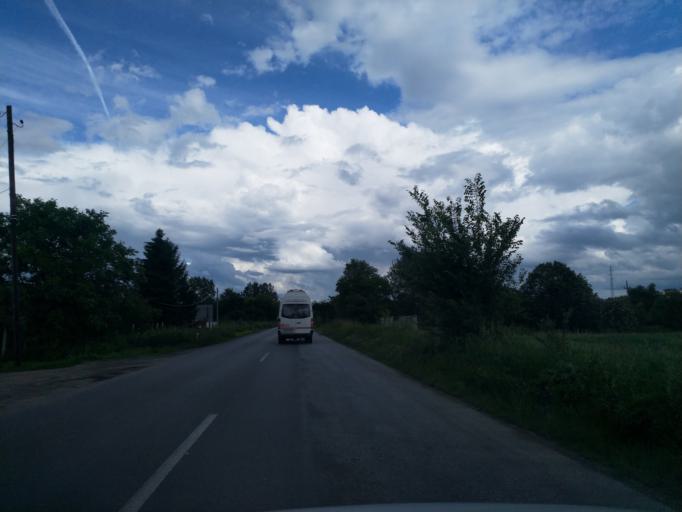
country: RS
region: Central Serbia
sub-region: Pomoravski Okrug
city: Cuprija
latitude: 43.9429
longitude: 21.3518
